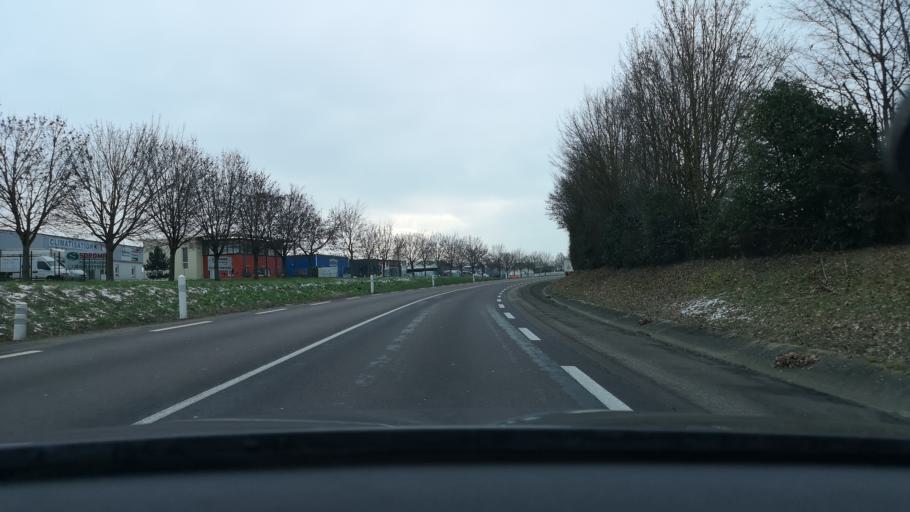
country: FR
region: Bourgogne
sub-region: Departement de Saone-et-Loire
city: Saint-Marcel
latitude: 46.7875
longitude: 4.9066
